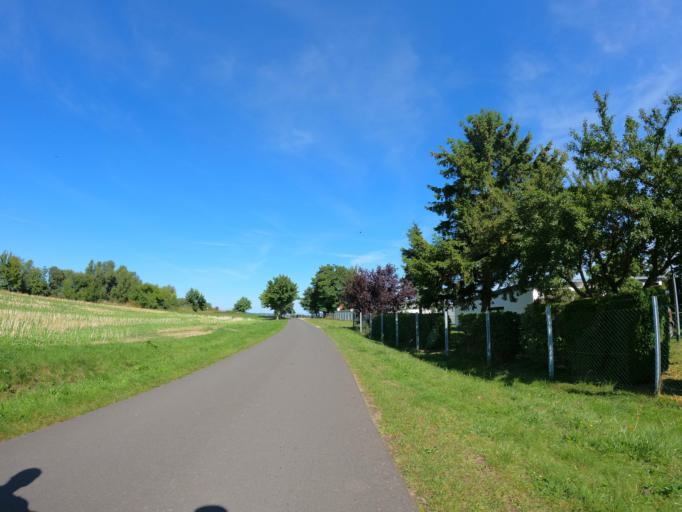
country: DE
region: Mecklenburg-Vorpommern
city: Prohn
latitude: 54.3786
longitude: 13.0473
